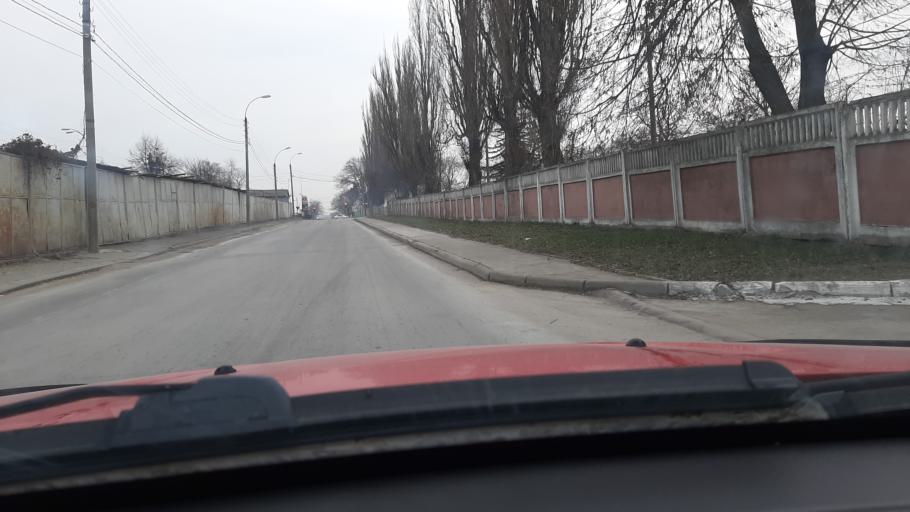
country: MD
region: Chisinau
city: Vatra
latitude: 47.0362
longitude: 28.7923
